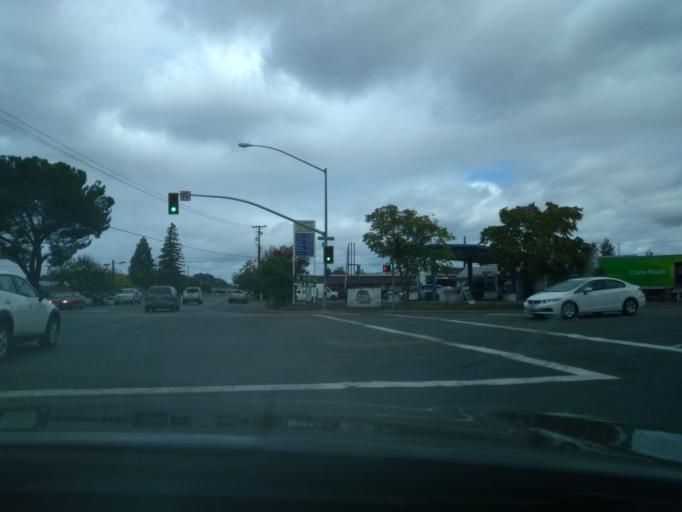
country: US
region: California
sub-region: Mendocino County
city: Ukiah
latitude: 39.1927
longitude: -123.2068
